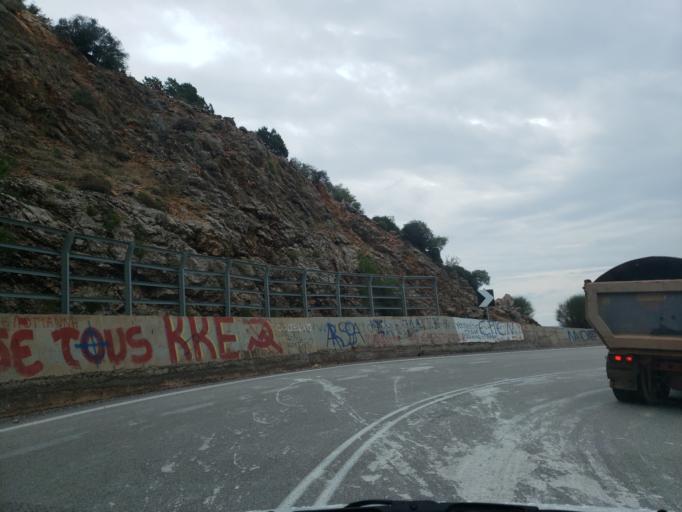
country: GR
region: Central Greece
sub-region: Nomos Fokidos
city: Amfissa
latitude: 38.5597
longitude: 22.4060
